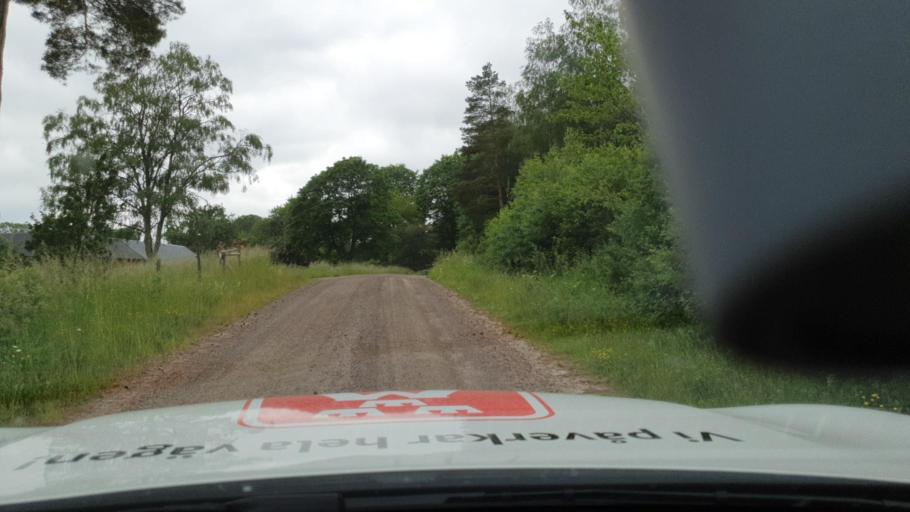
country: SE
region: Vaestra Goetaland
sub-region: Hjo Kommun
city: Hjo
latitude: 58.3445
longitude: 14.3073
